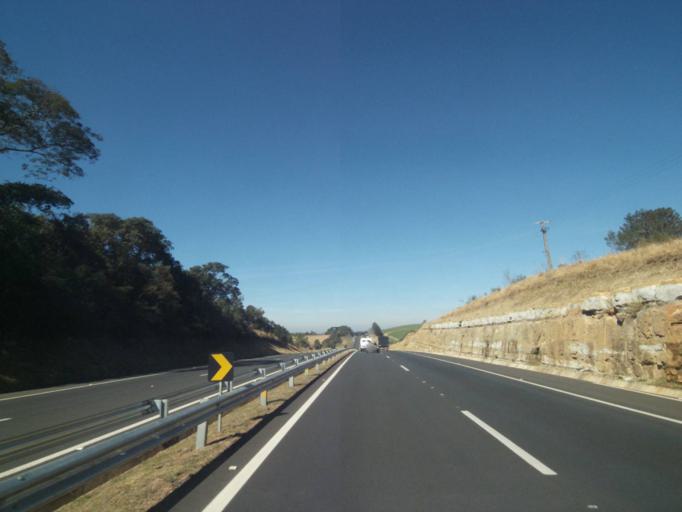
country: BR
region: Parana
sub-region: Carambei
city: Carambei
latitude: -24.8641
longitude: -50.4471
